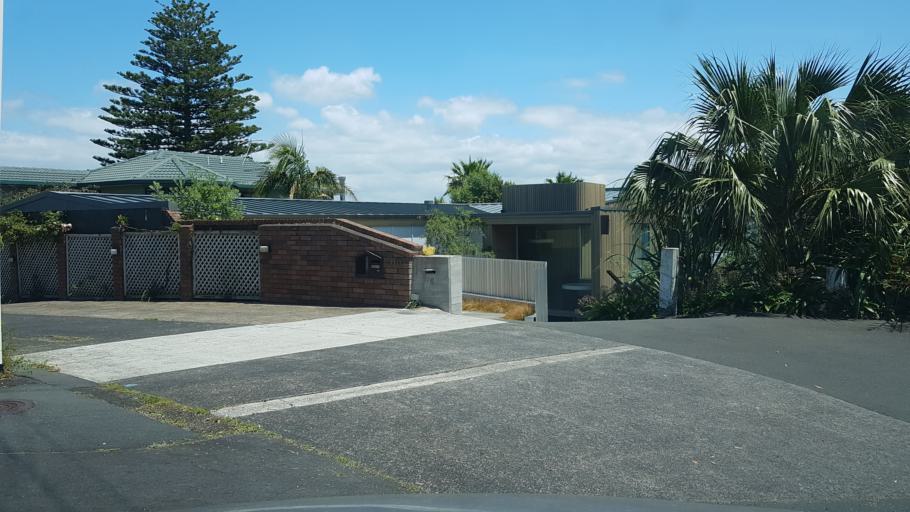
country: NZ
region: Auckland
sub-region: Auckland
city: North Shore
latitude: -36.8280
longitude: 174.7730
